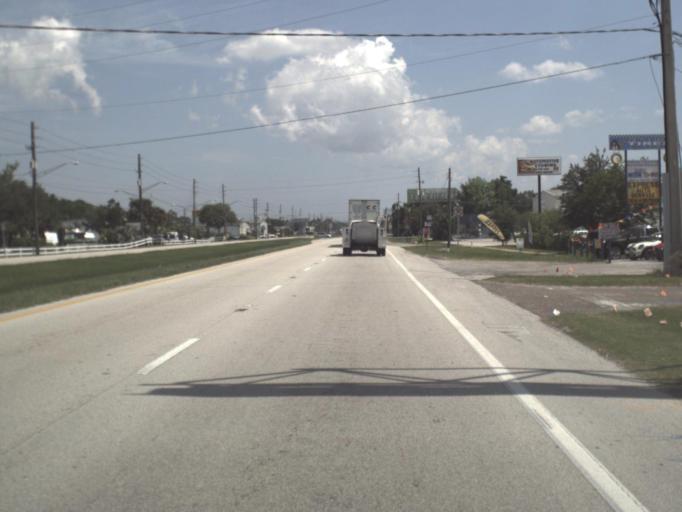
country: US
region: Florida
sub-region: Duval County
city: Jacksonville
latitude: 30.2725
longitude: -81.6230
